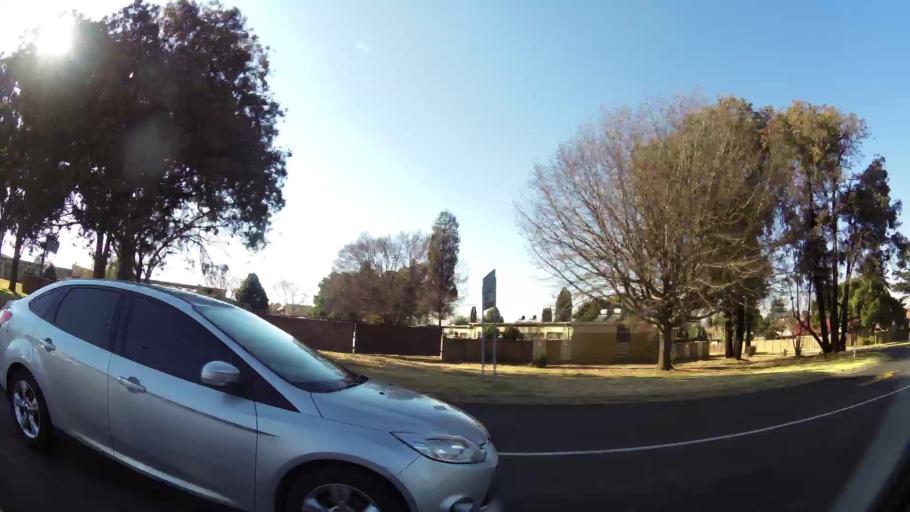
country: ZA
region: Gauteng
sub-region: Ekurhuleni Metropolitan Municipality
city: Germiston
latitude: -26.2896
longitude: 28.1199
